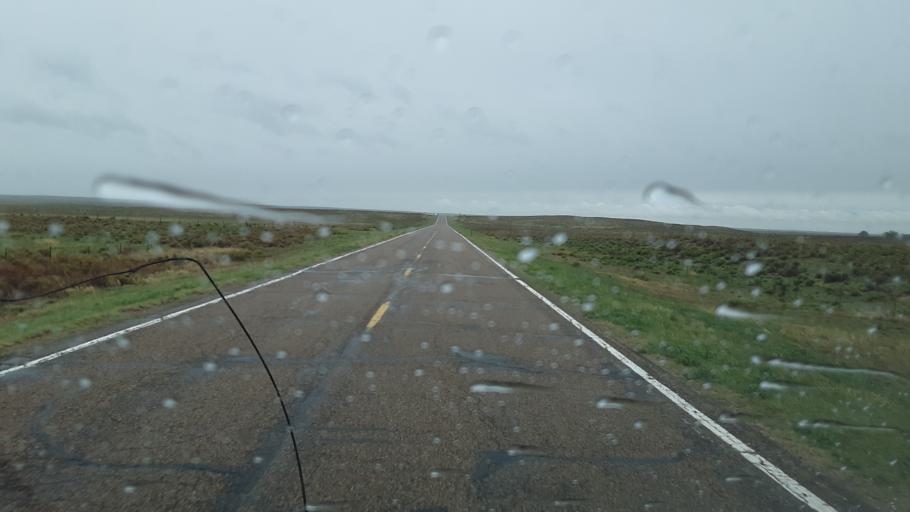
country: US
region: Colorado
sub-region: Lincoln County
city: Hugo
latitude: 38.8570
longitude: -103.1499
